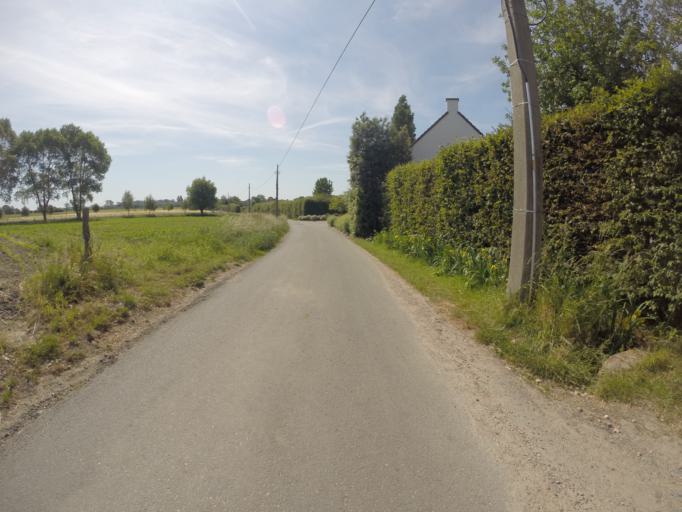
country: BE
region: Flanders
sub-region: Provincie West-Vlaanderen
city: Beernem
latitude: 51.1796
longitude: 3.3235
